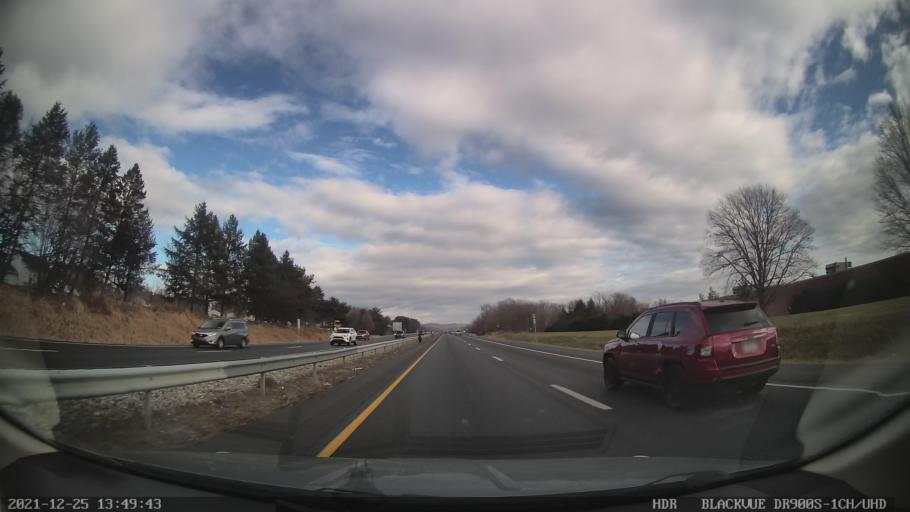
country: US
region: Pennsylvania
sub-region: Lancaster County
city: Mountville
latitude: 40.0484
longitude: -76.4092
